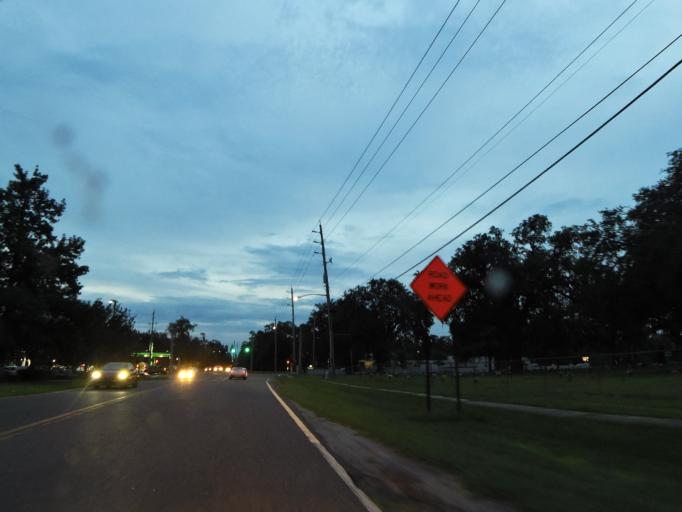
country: US
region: Florida
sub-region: Duval County
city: Jacksonville
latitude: 30.3003
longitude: -81.7678
